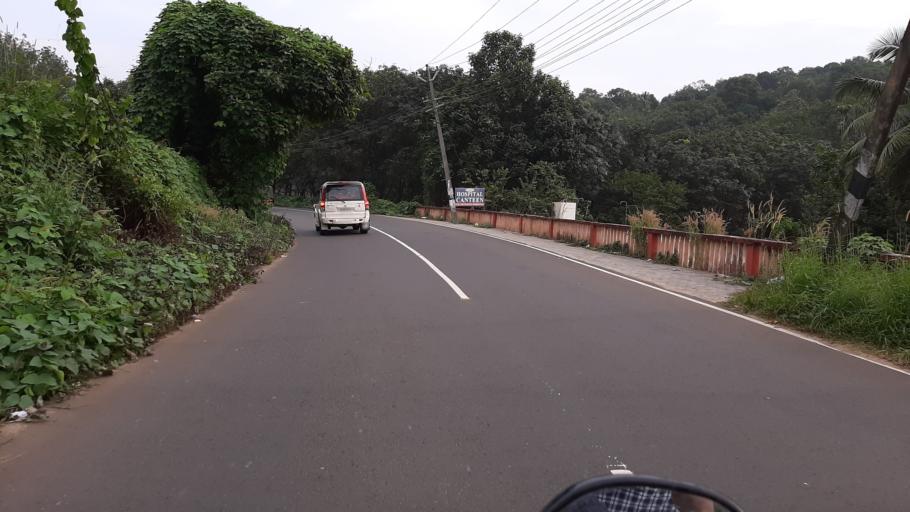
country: IN
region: Kerala
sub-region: Pattanamtitta
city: Pathanamthitta
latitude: 9.4486
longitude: 76.8724
